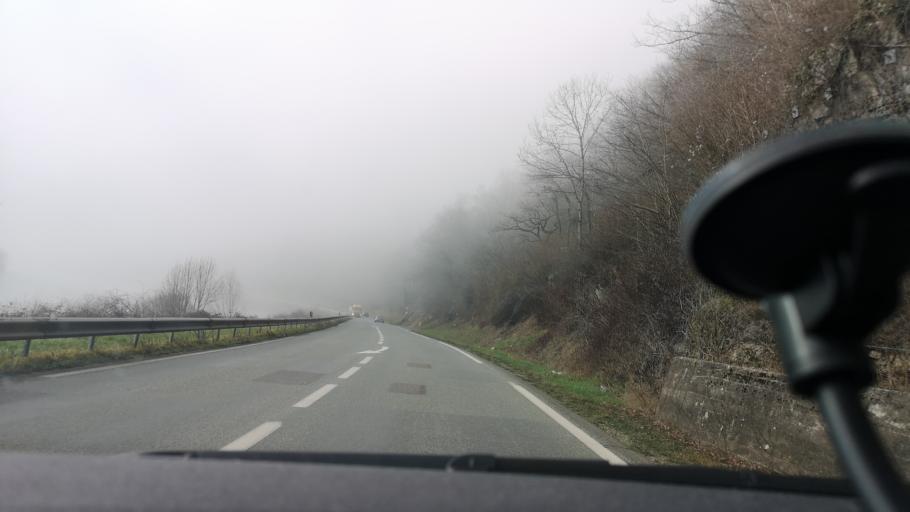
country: FR
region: Franche-Comte
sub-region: Departement du Doubs
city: Baume-les-Dames
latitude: 47.3723
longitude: 6.4244
